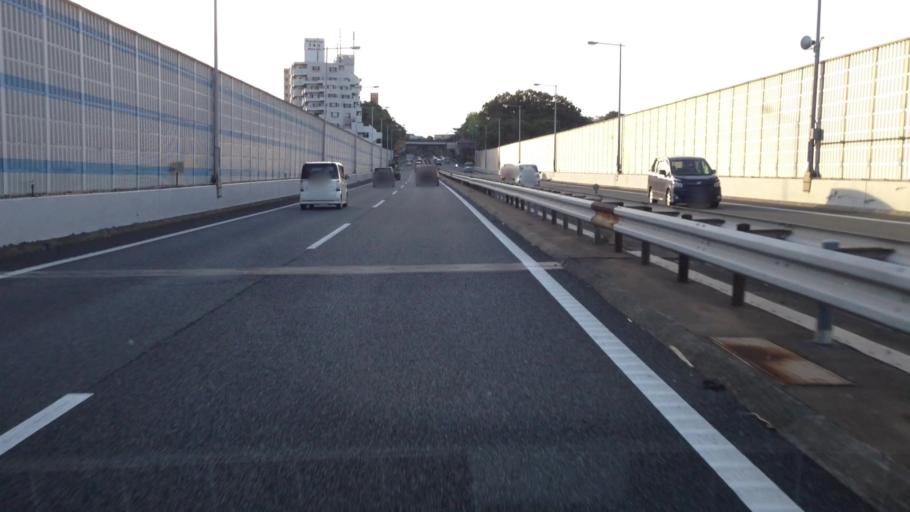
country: JP
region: Kanagawa
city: Kamakura
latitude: 35.3853
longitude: 139.5808
